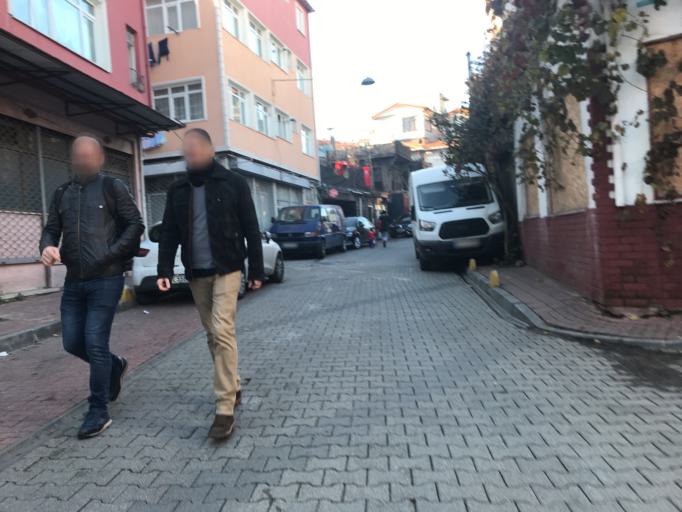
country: TR
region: Istanbul
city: Istanbul
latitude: 41.0247
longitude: 28.9582
